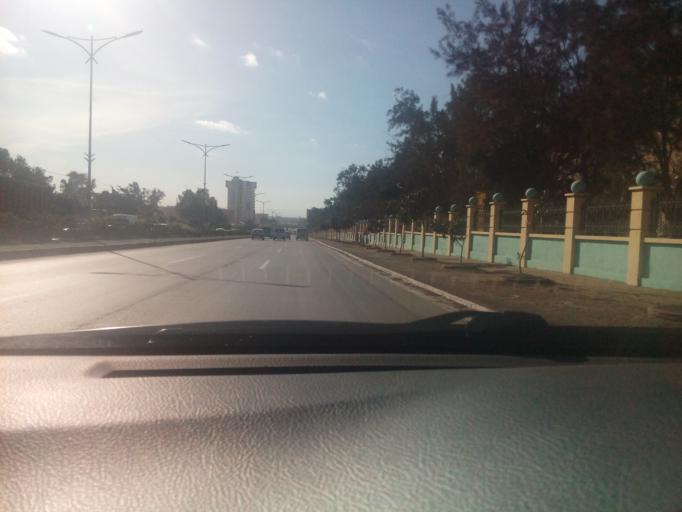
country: DZ
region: Oran
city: Oran
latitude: 35.6930
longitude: -0.6063
